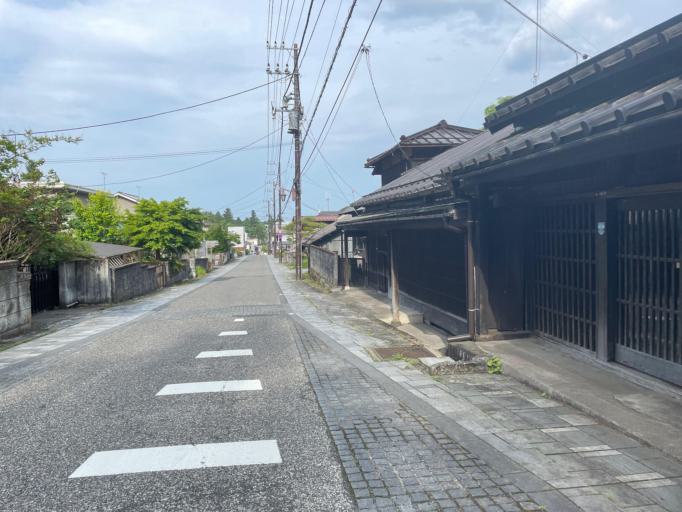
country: JP
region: Tochigi
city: Nikko
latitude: 36.7528
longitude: 139.5926
